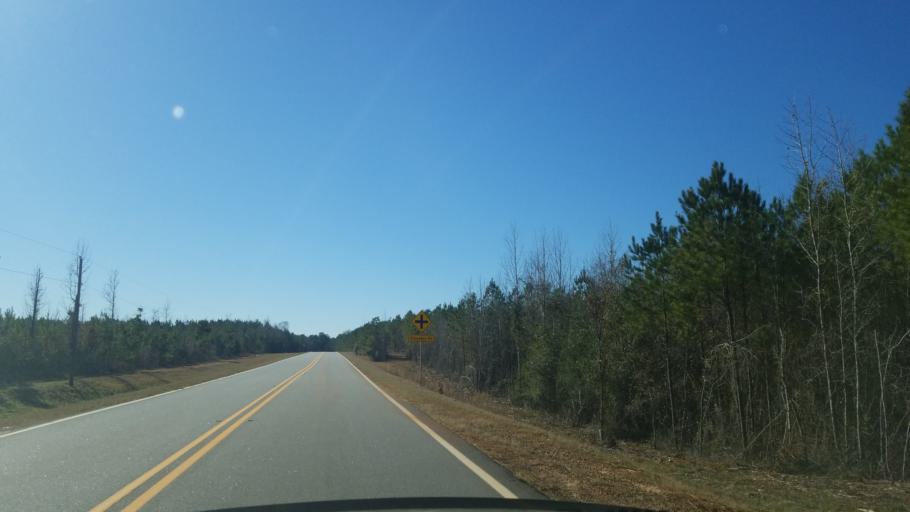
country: US
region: Georgia
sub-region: Talbot County
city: Sardis
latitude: 32.6370
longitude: -84.7189
